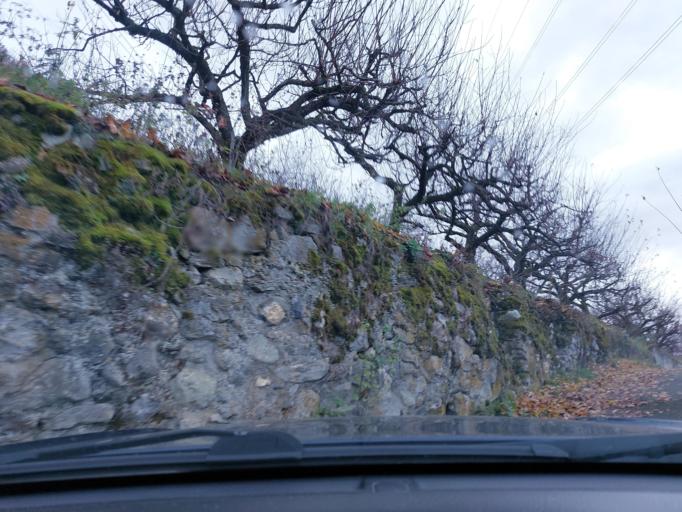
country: CH
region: Valais
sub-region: Martigny District
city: Saxon
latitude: 46.1437
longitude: 7.1823
